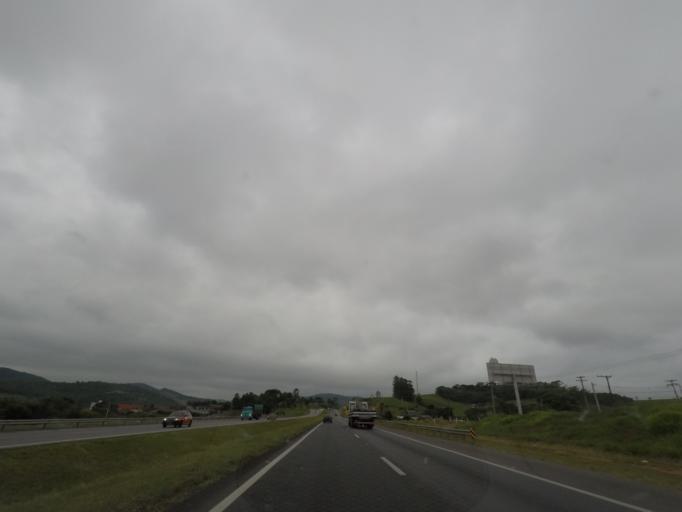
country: BR
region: Sao Paulo
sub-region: Bom Jesus Dos Perdoes
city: Bom Jesus dos Perdoes
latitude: -23.1683
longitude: -46.4141
